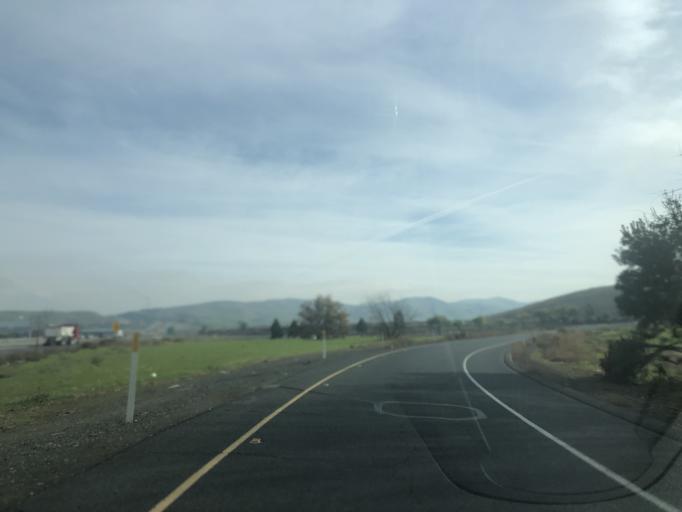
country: US
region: California
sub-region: Contra Costa County
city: Concord
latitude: 38.0088
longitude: -122.0257
